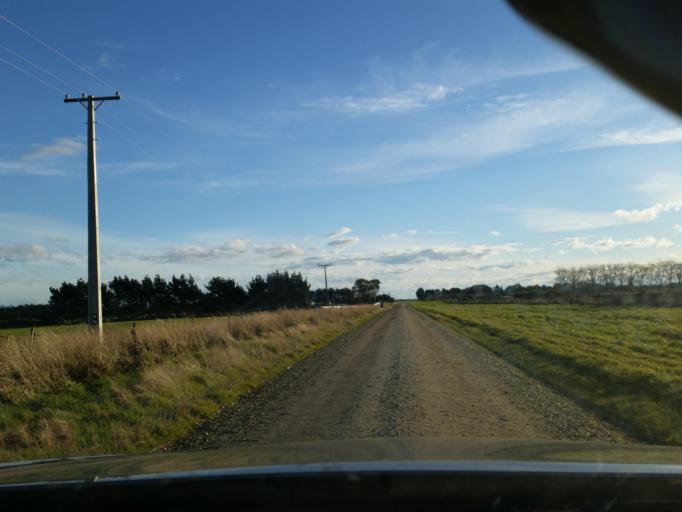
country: NZ
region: Southland
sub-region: Invercargill City
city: Invercargill
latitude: -46.3425
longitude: 168.6383
